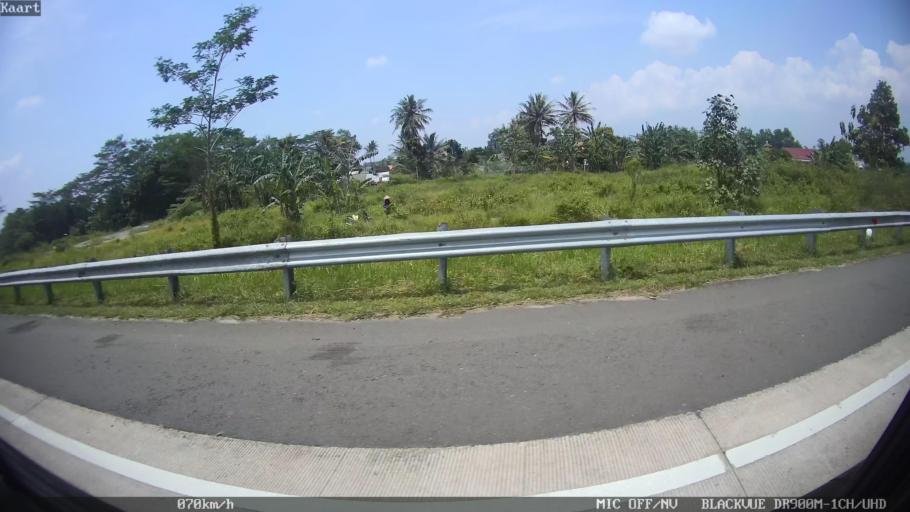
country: ID
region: Lampung
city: Kedaton
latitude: -5.3254
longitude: 105.2791
